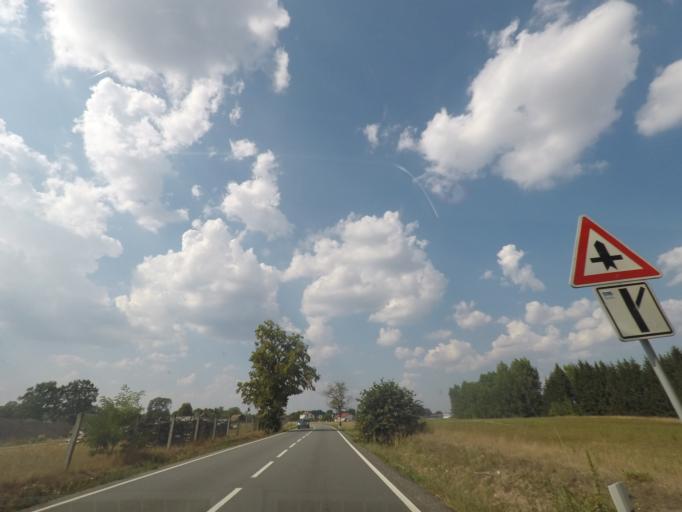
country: CZ
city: Borohradek
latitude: 50.1141
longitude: 16.0731
